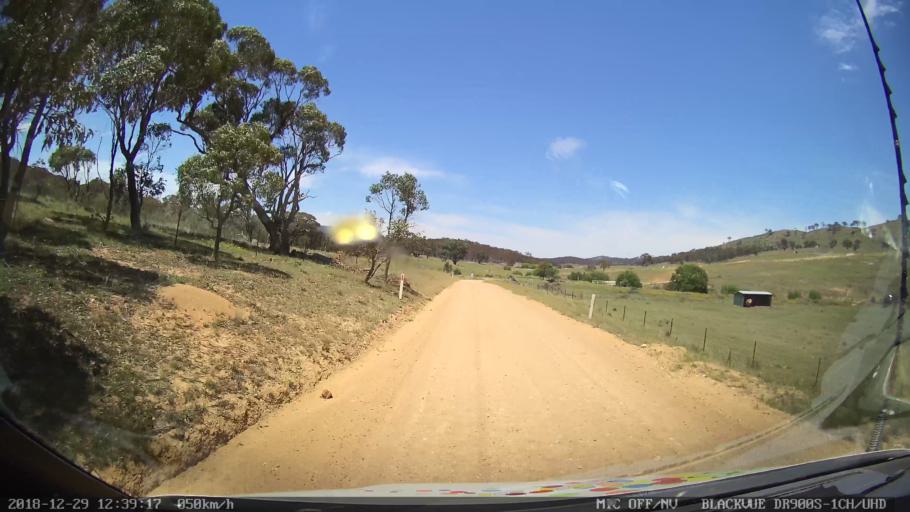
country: AU
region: Australian Capital Territory
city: Macarthur
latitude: -35.5961
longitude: 149.2277
